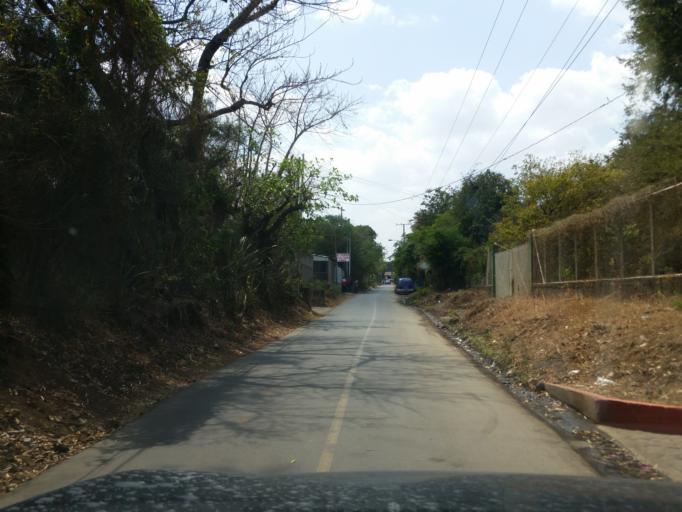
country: NI
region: Masaya
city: Ticuantepe
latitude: 12.0655
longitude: -86.2087
